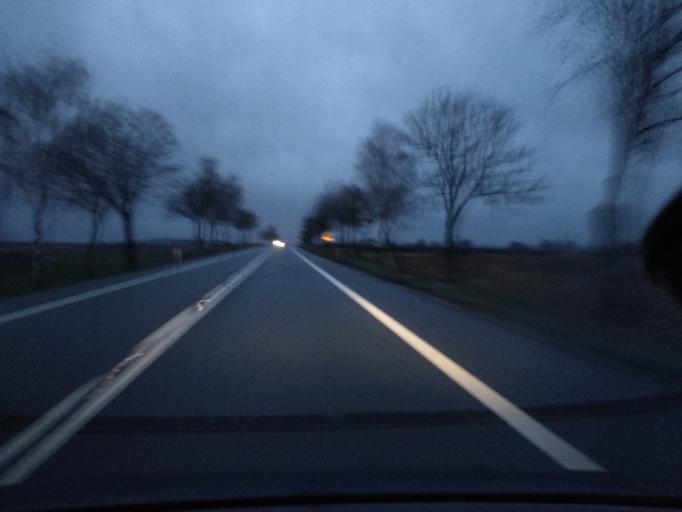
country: PL
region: Lower Silesian Voivodeship
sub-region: Powiat sredzki
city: Miekinia
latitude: 51.1608
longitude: 16.7039
